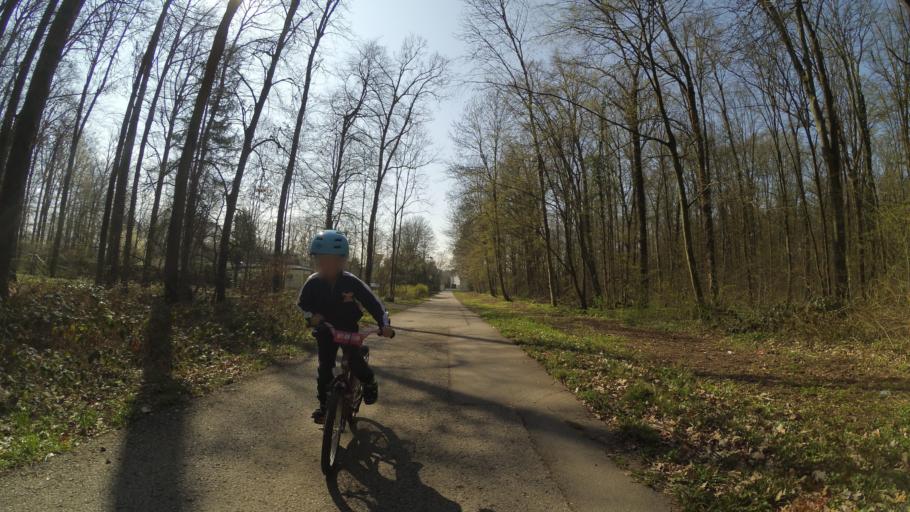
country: DE
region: Baden-Wuerttemberg
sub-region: Regierungsbezirk Stuttgart
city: Neckarsulm
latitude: 49.2093
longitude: 9.2414
